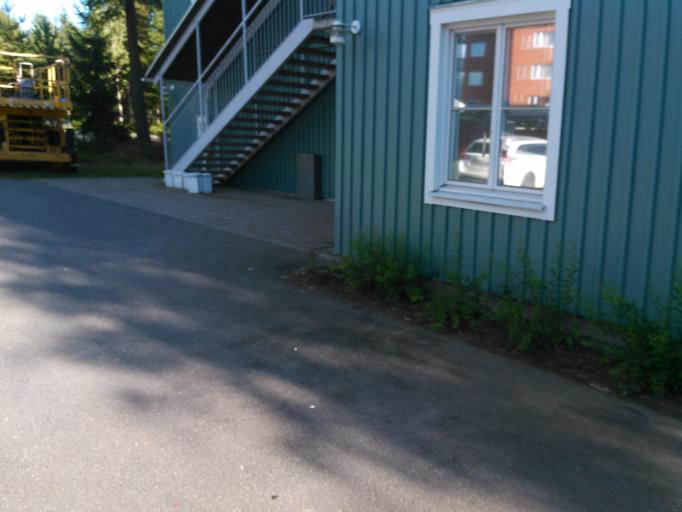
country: SE
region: Vaesterbotten
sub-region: Umea Kommun
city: Ersmark
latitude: 63.8247
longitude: 20.3253
